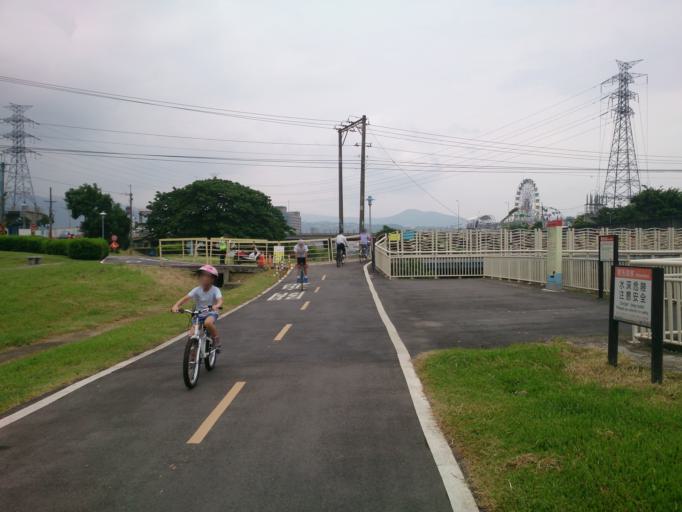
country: TW
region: Taipei
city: Taipei
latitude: 25.0979
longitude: 121.5109
